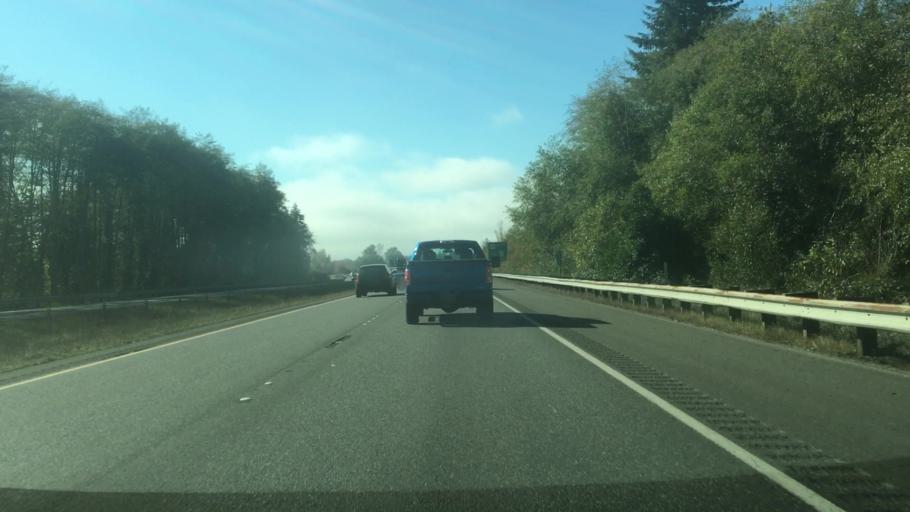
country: US
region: Washington
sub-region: Grays Harbor County
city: Montesano
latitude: 46.9791
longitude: -123.5898
